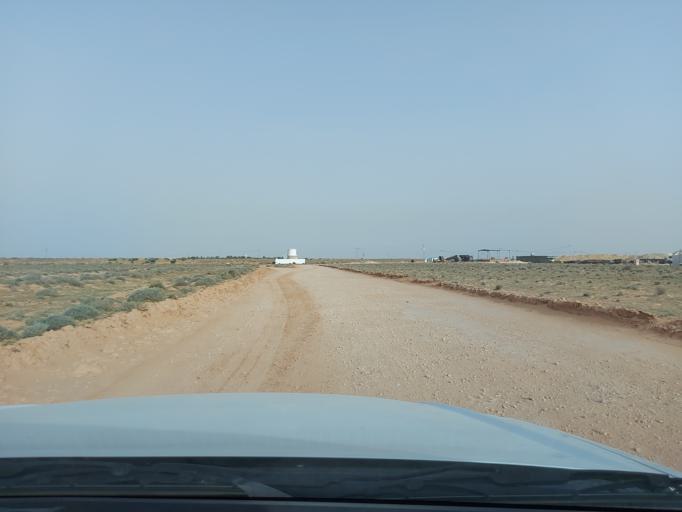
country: TN
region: Madanin
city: Medenine
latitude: 33.2647
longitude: 10.5707
